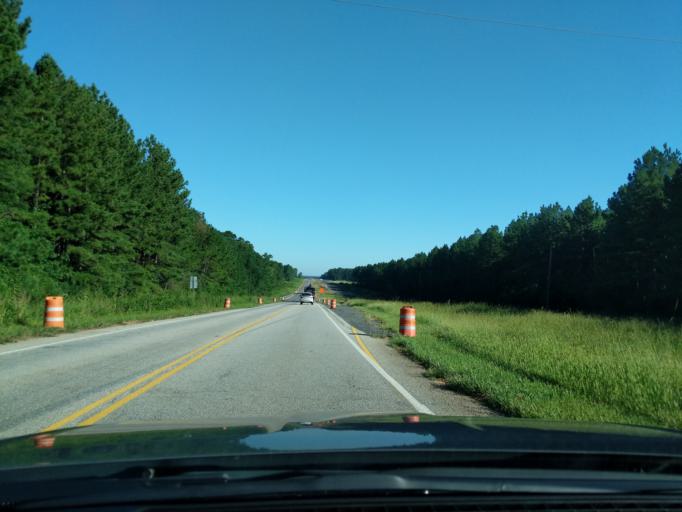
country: US
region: Georgia
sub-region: McDuffie County
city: Thomson
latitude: 33.5501
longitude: -82.5106
